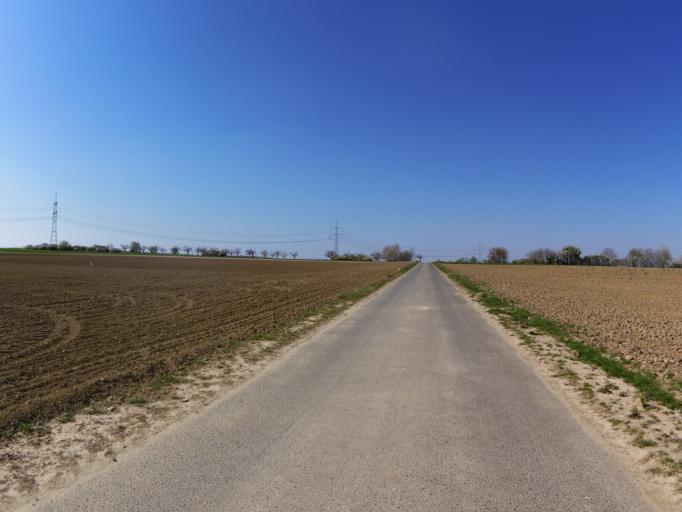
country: DE
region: Bavaria
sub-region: Regierungsbezirk Unterfranken
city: Biebelried
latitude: 49.8191
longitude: 10.0923
